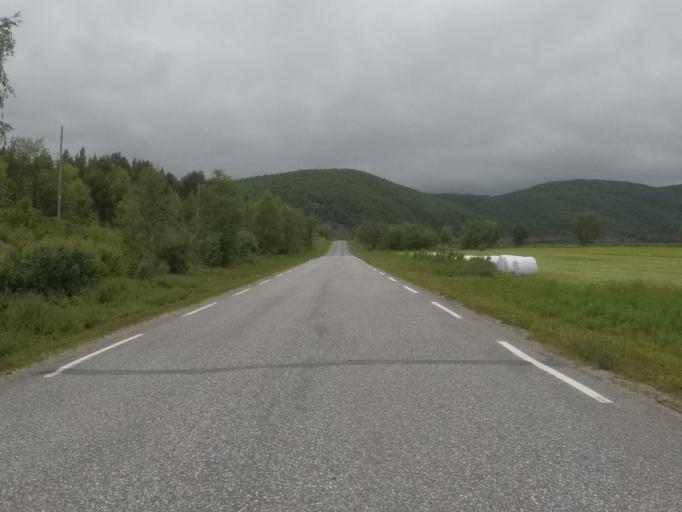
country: NO
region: Finnmark Fylke
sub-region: Karasjok
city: Karasjohka
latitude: 69.6554
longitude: 25.9080
